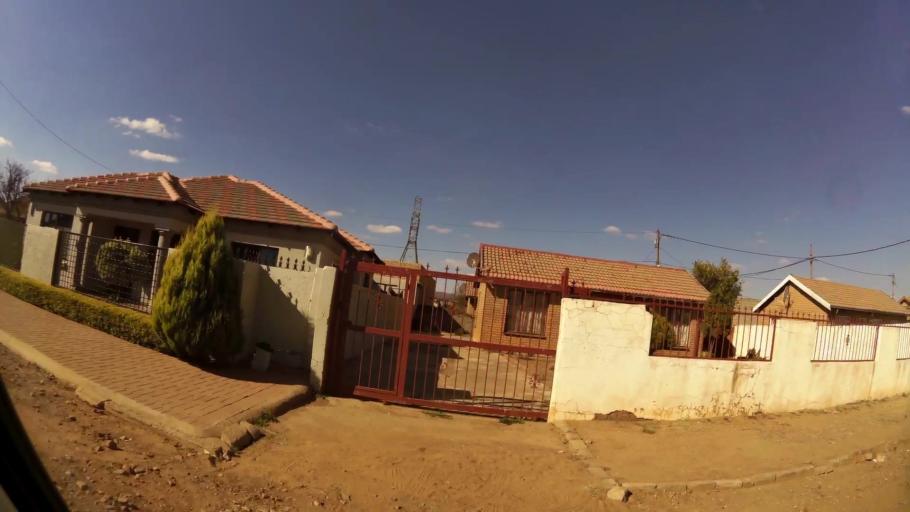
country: ZA
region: Gauteng
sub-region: City of Tshwane Metropolitan Municipality
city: Cullinan
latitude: -25.7164
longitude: 28.3969
